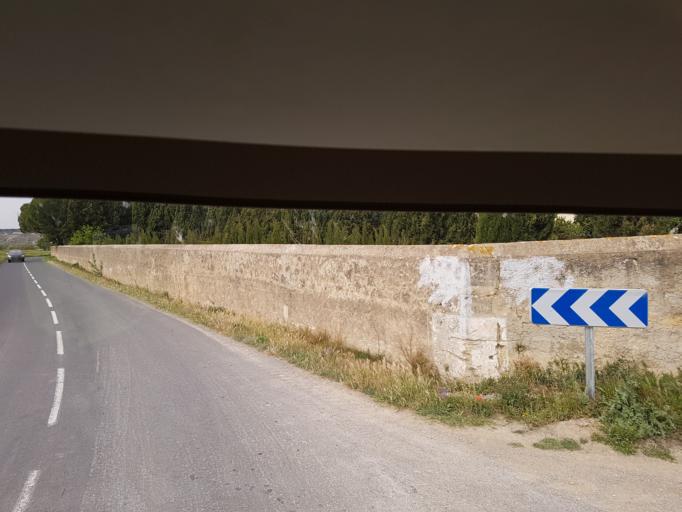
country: FR
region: Languedoc-Roussillon
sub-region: Departement de l'Herault
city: Lespignan
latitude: 43.2576
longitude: 3.1603
